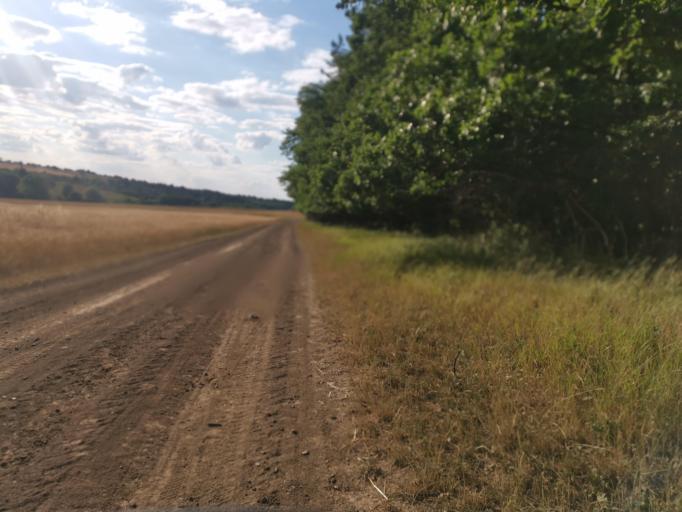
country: SK
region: Trnavsky
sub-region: Okres Skalica
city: Skalica
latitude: 48.8223
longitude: 17.2612
